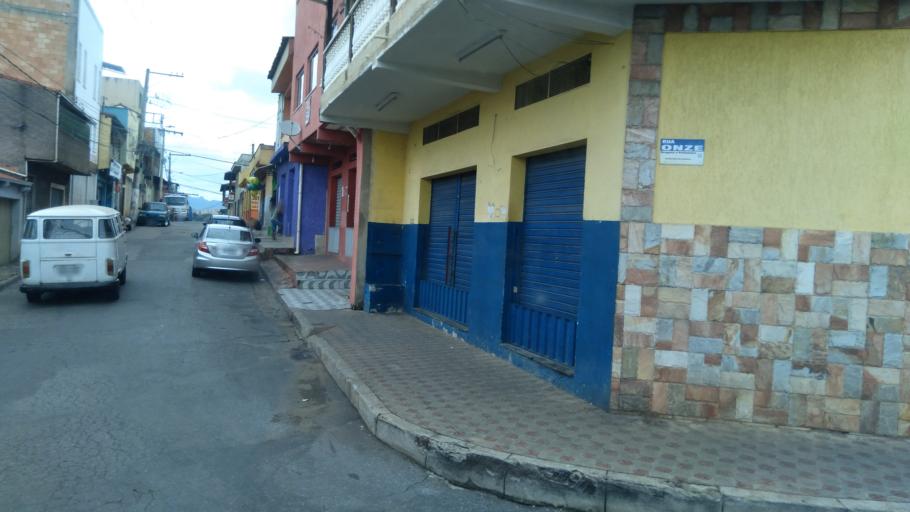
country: BR
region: Minas Gerais
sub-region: Belo Horizonte
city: Belo Horizonte
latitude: -19.8489
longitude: -43.8899
